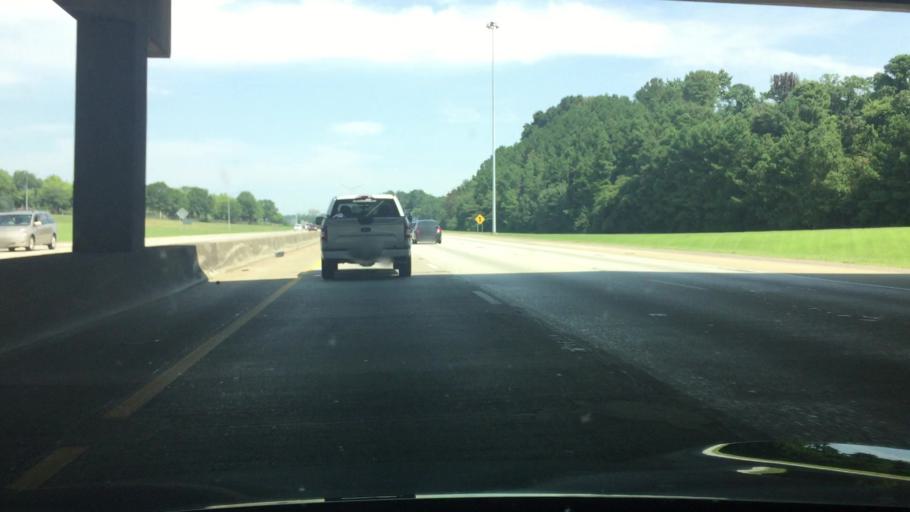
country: US
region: Alabama
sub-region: Jefferson County
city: Homewood
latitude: 33.4501
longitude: -86.8180
